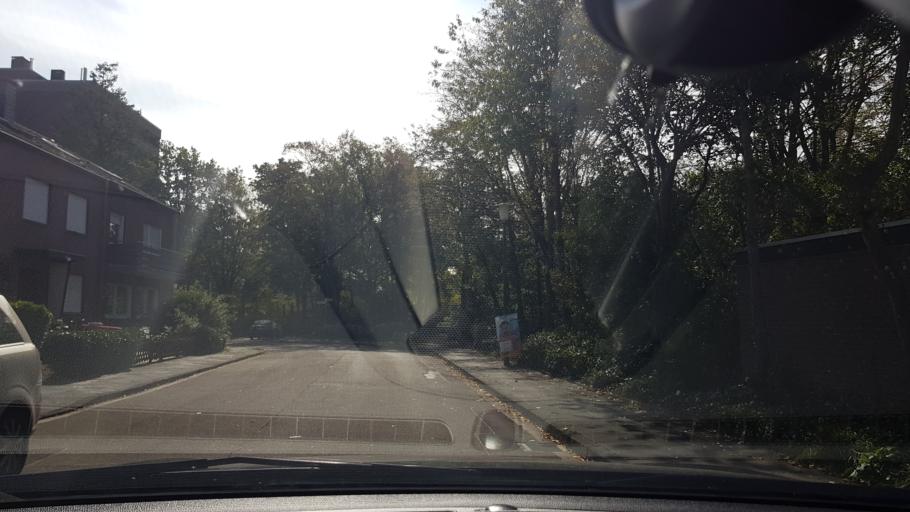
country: DE
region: North Rhine-Westphalia
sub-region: Regierungsbezirk Dusseldorf
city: Neuss
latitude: 51.1536
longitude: 6.6975
